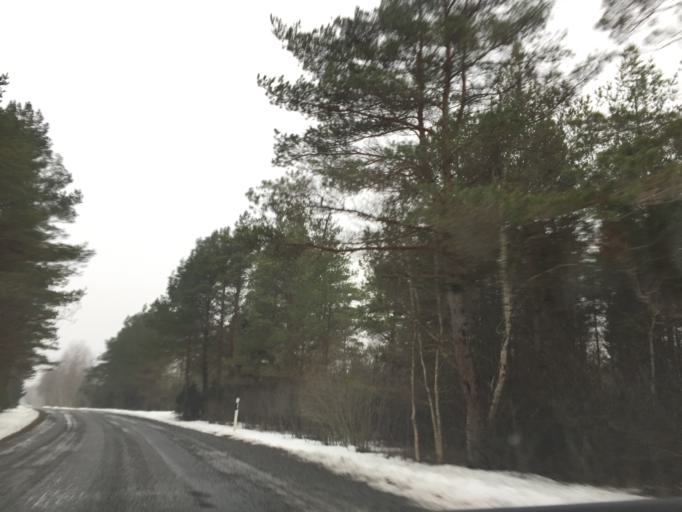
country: EE
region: Saare
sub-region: Orissaare vald
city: Orissaare
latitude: 58.3924
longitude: 22.8548
